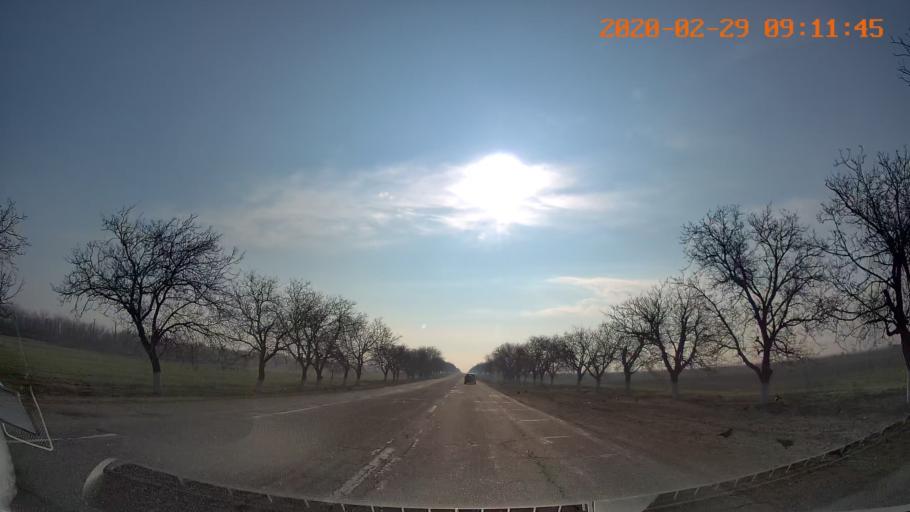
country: MD
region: Telenesti
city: Slobozia
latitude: 46.8324
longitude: 29.8053
